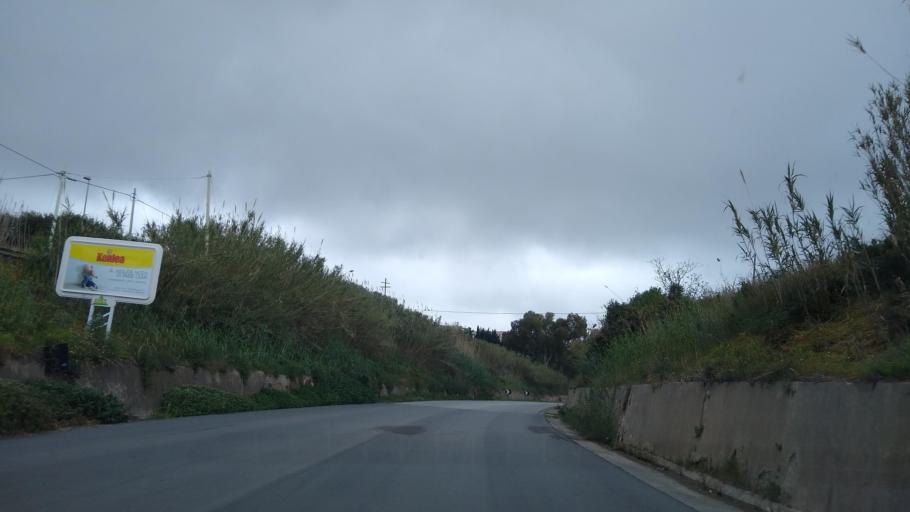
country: IT
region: Sicily
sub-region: Trapani
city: Alcamo
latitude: 37.9871
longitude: 12.9531
